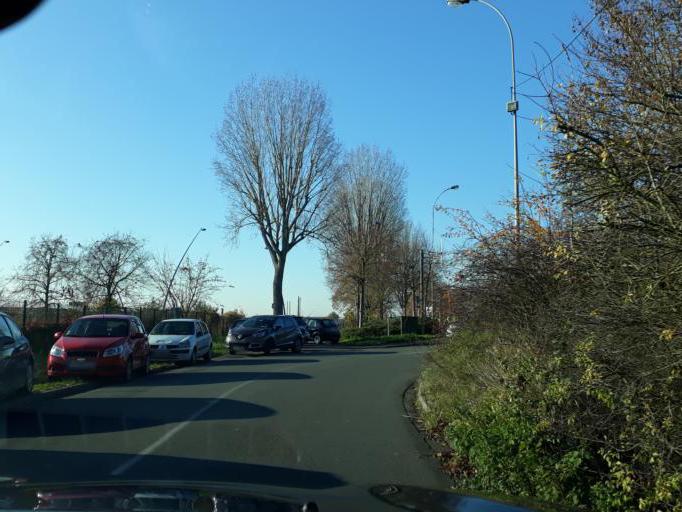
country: FR
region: Nord-Pas-de-Calais
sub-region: Departement du Nord
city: Dechy
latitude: 50.3476
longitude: 3.1172
